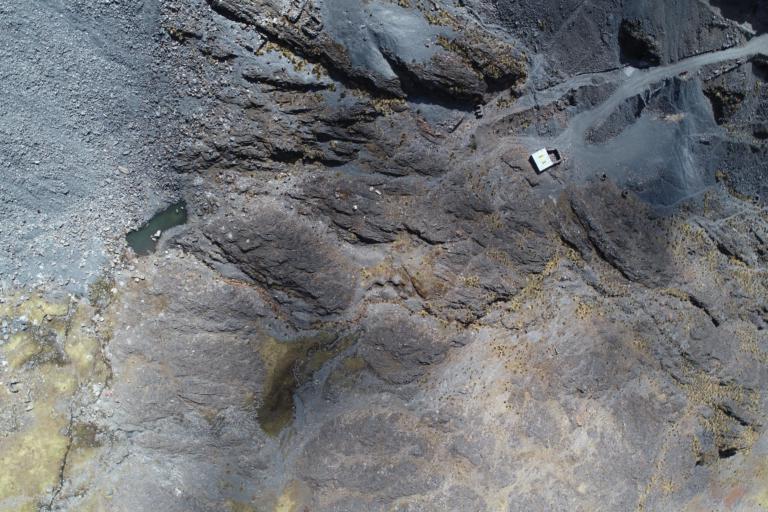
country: BO
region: La Paz
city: Sorata
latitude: -15.6709
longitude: -68.5633
